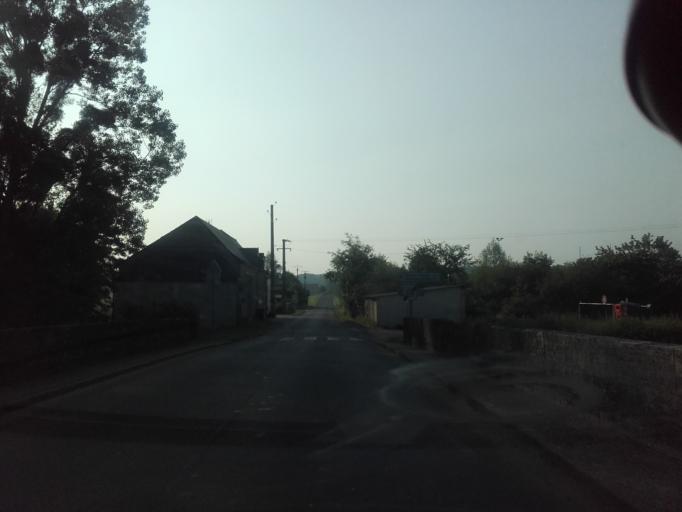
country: FR
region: Centre
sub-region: Departement d'Indre-et-Loire
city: Reugny
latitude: 47.4512
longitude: 0.8750
